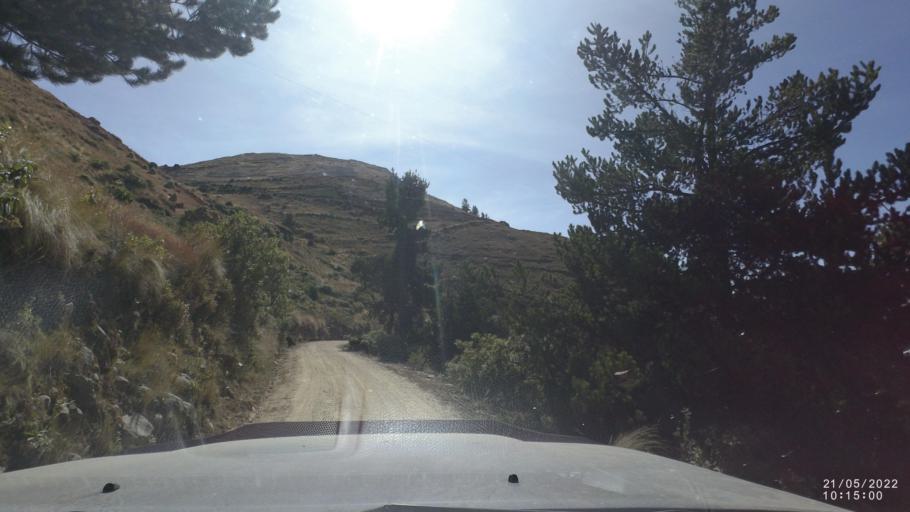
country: BO
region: Cochabamba
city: Colomi
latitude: -17.3317
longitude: -65.9692
